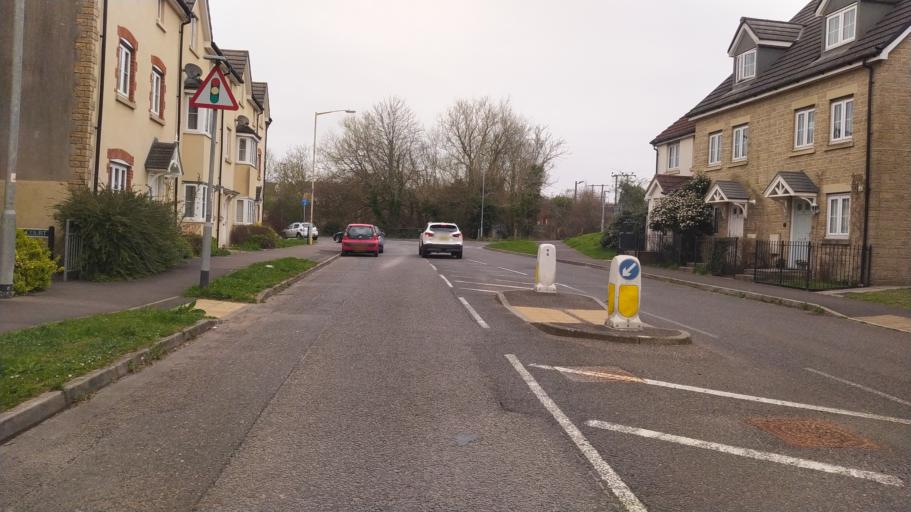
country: GB
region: England
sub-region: Somerset
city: Frome
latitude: 51.2304
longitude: -2.3061
